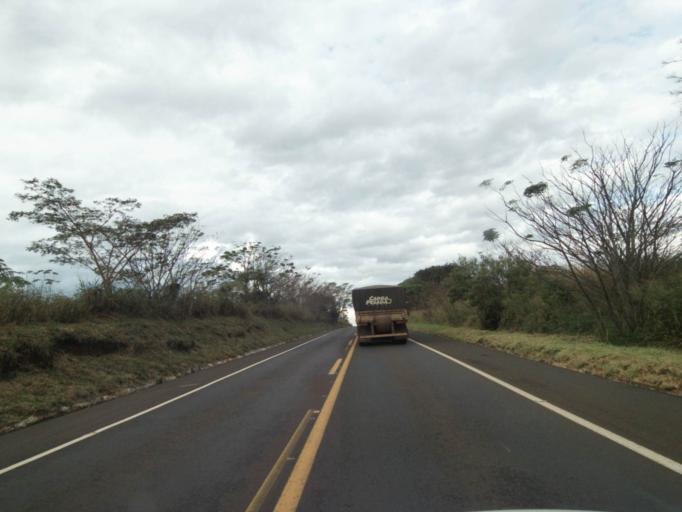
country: PY
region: Canindeyu
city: Salto del Guaira
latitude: -24.0830
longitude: -54.0901
